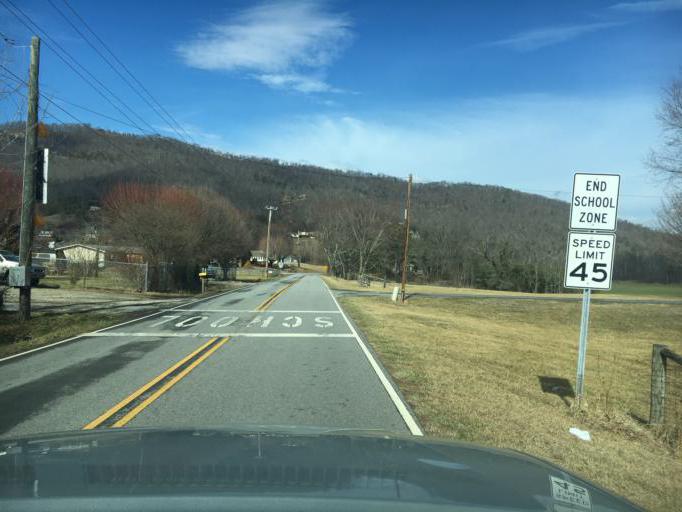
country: US
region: North Carolina
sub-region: Haywood County
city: Clyde
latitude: 35.4874
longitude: -82.8862
